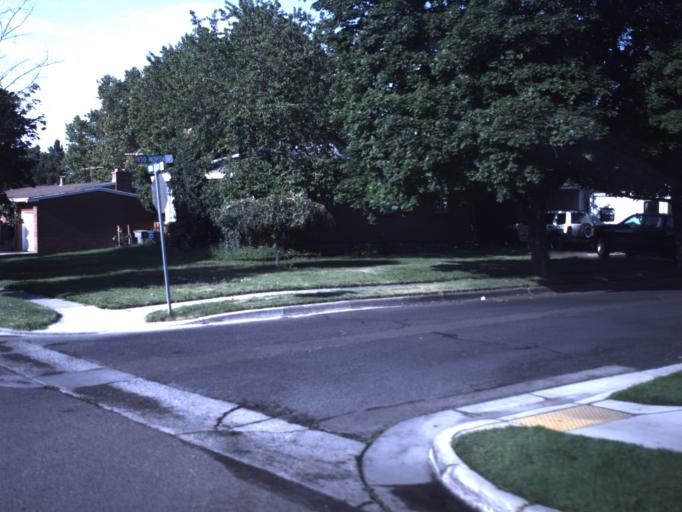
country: US
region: Utah
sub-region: Utah County
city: American Fork
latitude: 40.3940
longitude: -111.7959
